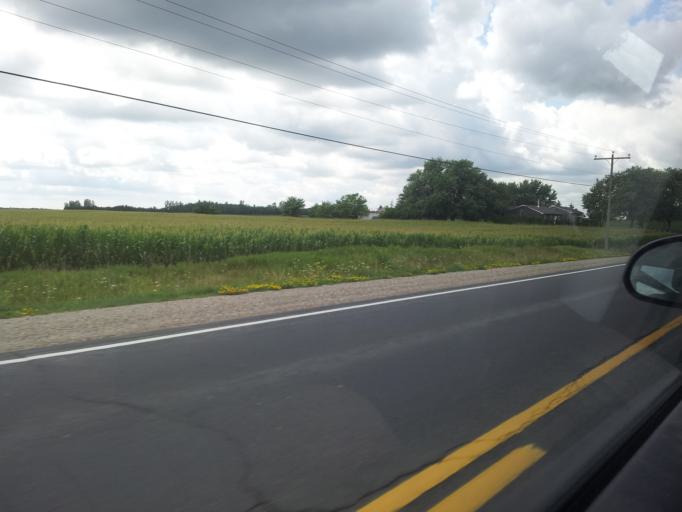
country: CA
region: Ontario
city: Stratford
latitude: 43.3697
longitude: -80.8552
